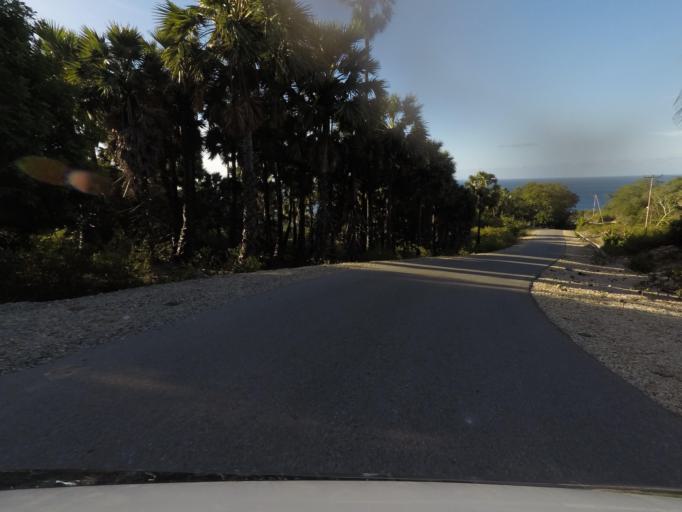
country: TL
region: Lautem
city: Lospalos
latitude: -8.3619
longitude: 127.0535
